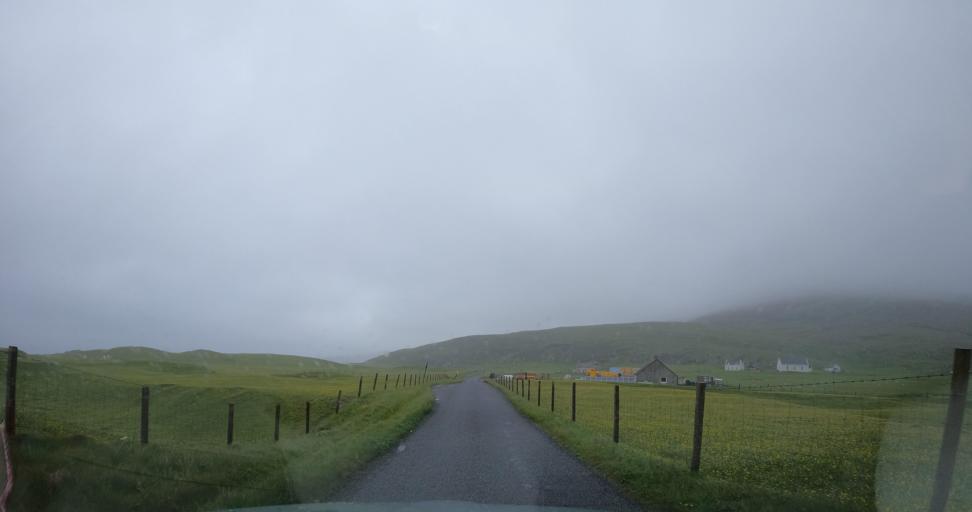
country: GB
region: Scotland
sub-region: Eilean Siar
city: Barra
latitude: 56.9845
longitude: -7.5096
